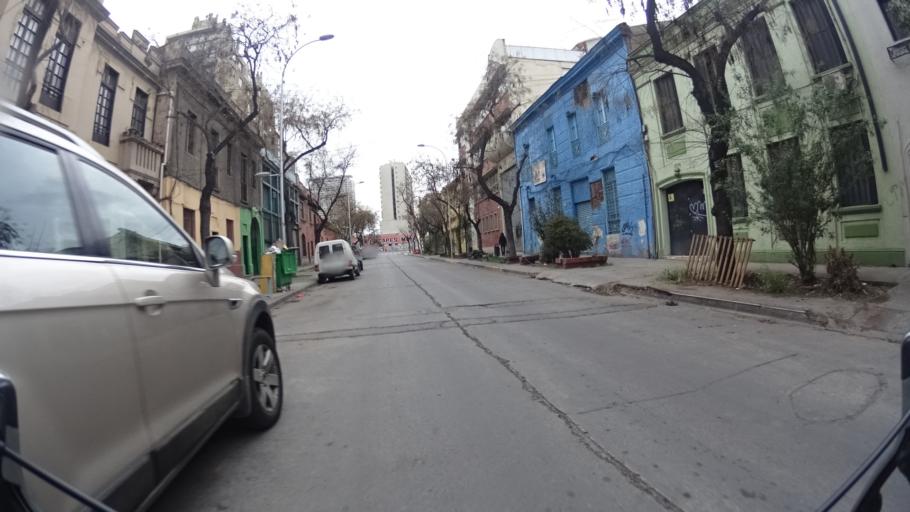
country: CL
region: Santiago Metropolitan
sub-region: Provincia de Santiago
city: Santiago
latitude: -33.4552
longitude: -70.6595
